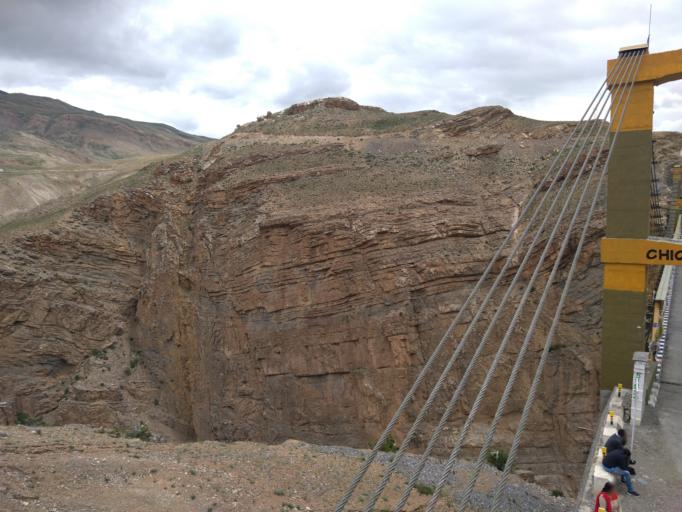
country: IN
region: Himachal Pradesh
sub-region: Kulu
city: Manali
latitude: 32.3440
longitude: 77.9973
